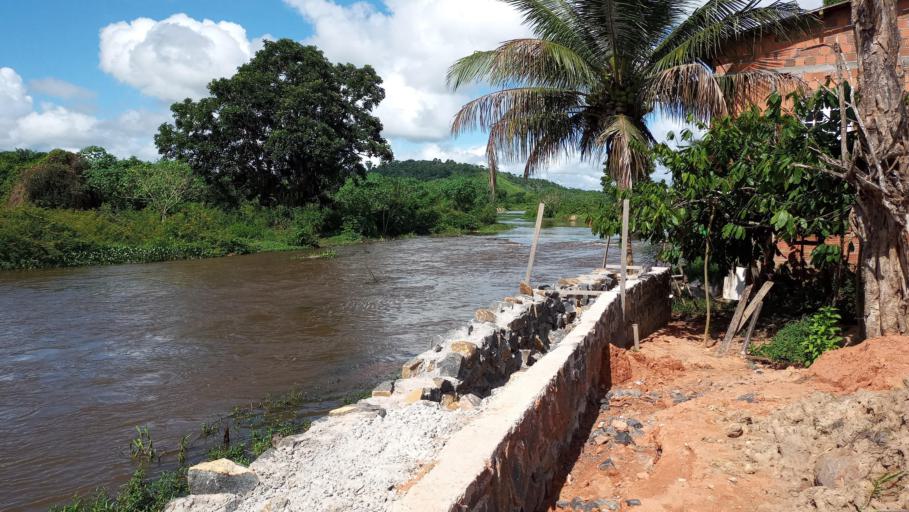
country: BR
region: Bahia
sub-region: Ubata
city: Ubata
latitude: -14.2183
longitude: -39.5179
